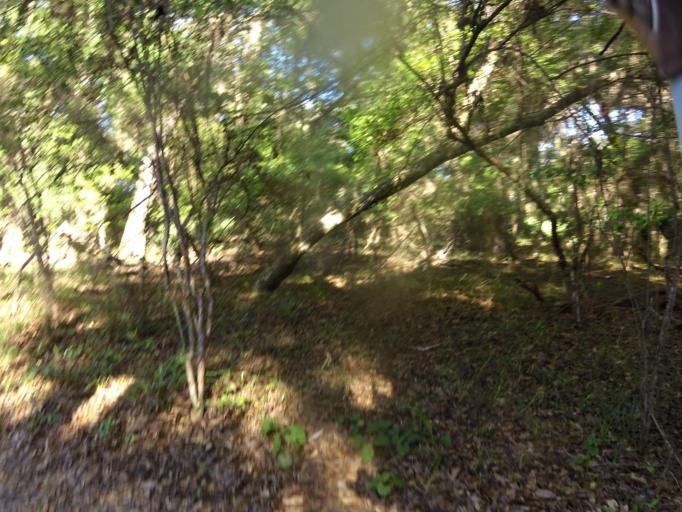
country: US
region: Florida
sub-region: Saint Johns County
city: Villano Beach
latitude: 30.0198
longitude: -81.3341
